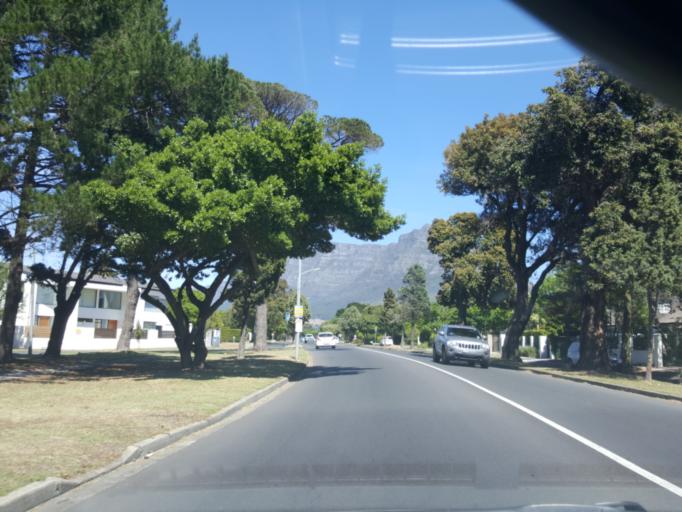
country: ZA
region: Western Cape
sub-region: City of Cape Town
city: Rosebank
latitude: -33.9426
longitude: 18.4974
